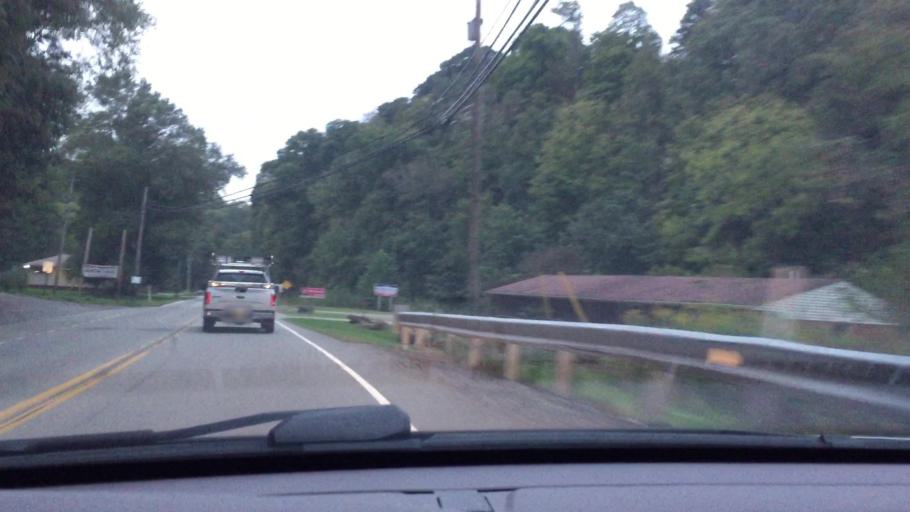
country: US
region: Pennsylvania
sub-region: Westmoreland County
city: West Newton
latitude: 40.2006
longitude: -79.7901
